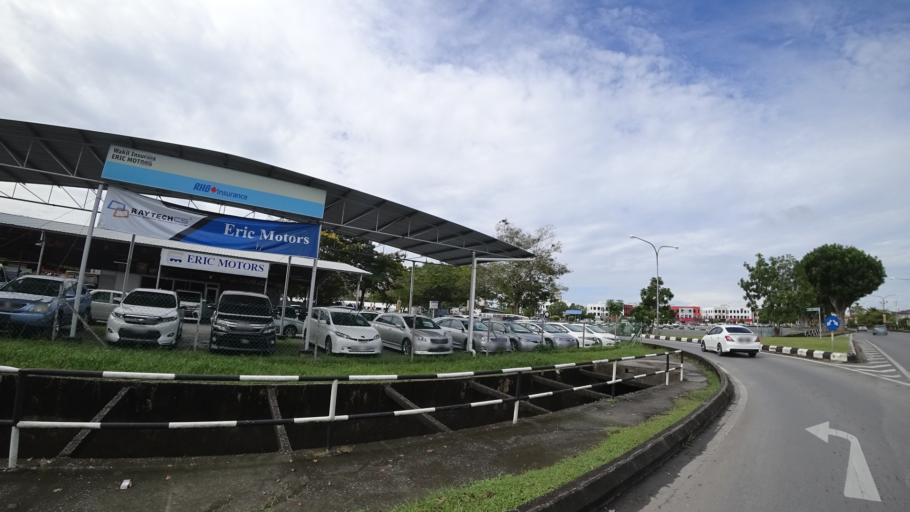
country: MY
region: Sarawak
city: Miri
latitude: 4.4176
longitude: 114.0141
